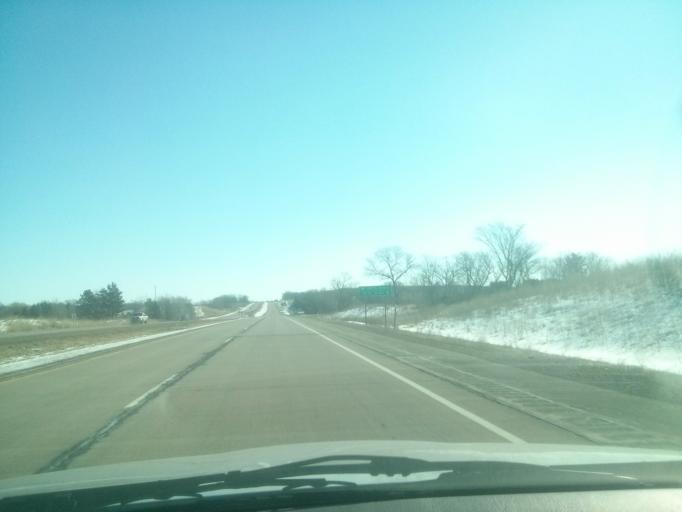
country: US
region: Wisconsin
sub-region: Saint Croix County
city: Somerset
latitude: 45.1227
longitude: -92.6153
